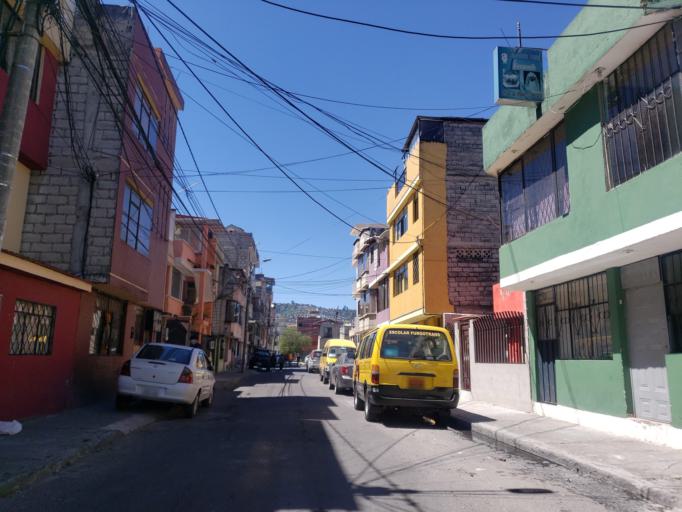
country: EC
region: Pichincha
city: Quito
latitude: -0.2655
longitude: -78.5401
